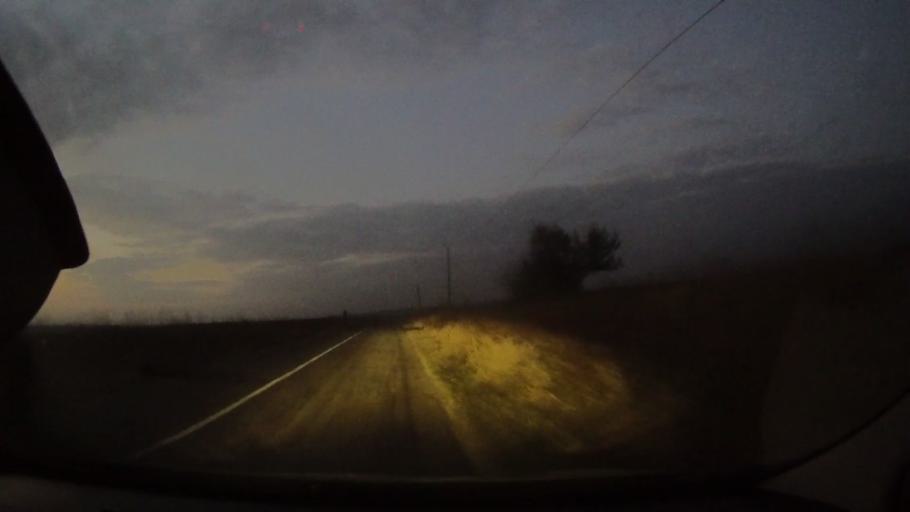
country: RO
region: Constanta
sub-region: Comuna Aliman
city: Aliman
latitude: 44.1544
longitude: 27.8360
